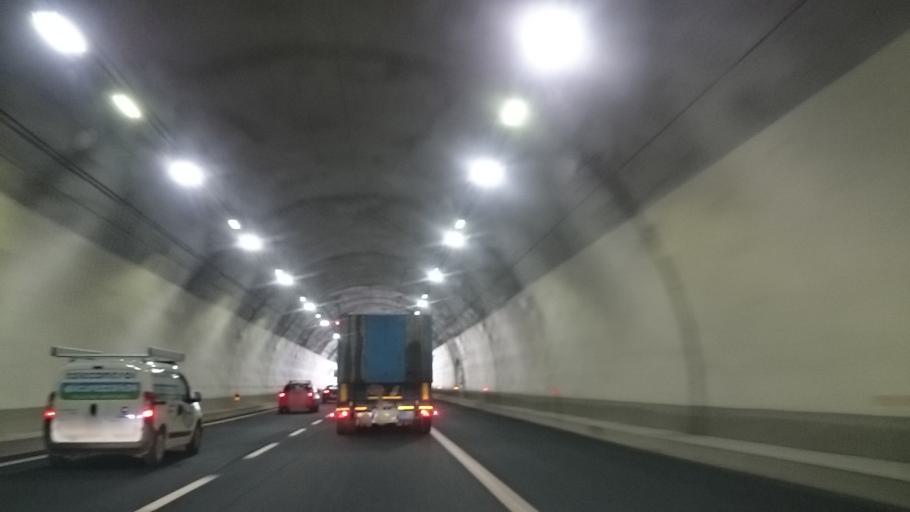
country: IT
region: Emilia-Romagna
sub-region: Provincia di Bologna
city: Grizzana
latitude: 44.2841
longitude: 11.2010
